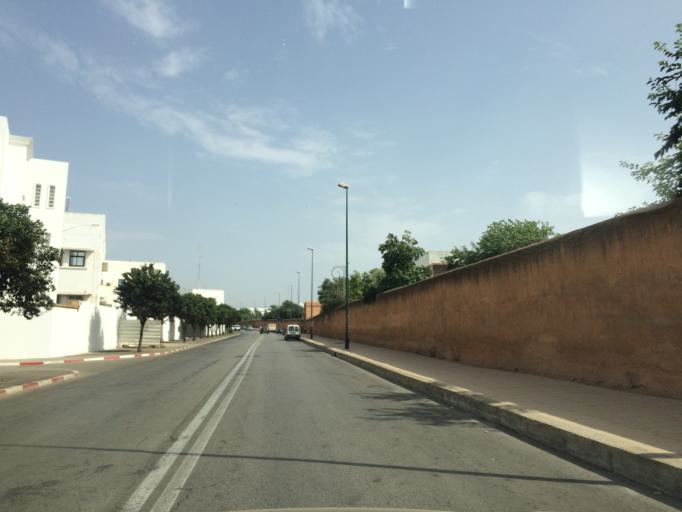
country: MA
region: Rabat-Sale-Zemmour-Zaer
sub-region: Rabat
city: Rabat
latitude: 34.0110
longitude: -6.8312
